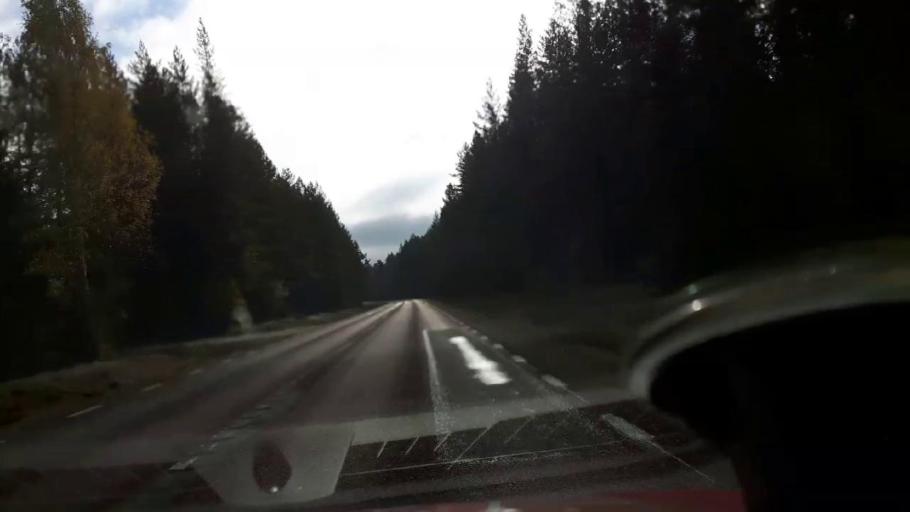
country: SE
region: Gaevleborg
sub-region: Ljusdals Kommun
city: Farila
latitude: 61.8823
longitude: 15.7086
